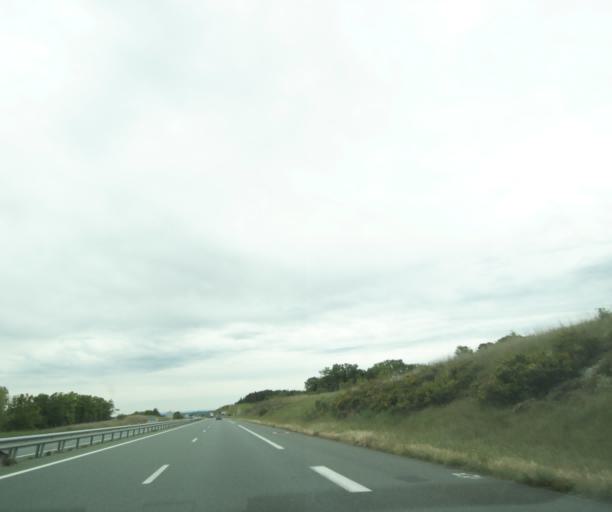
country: FR
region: Midi-Pyrenees
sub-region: Departement du Lot
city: Le Vigan
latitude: 44.6649
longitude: 1.5692
